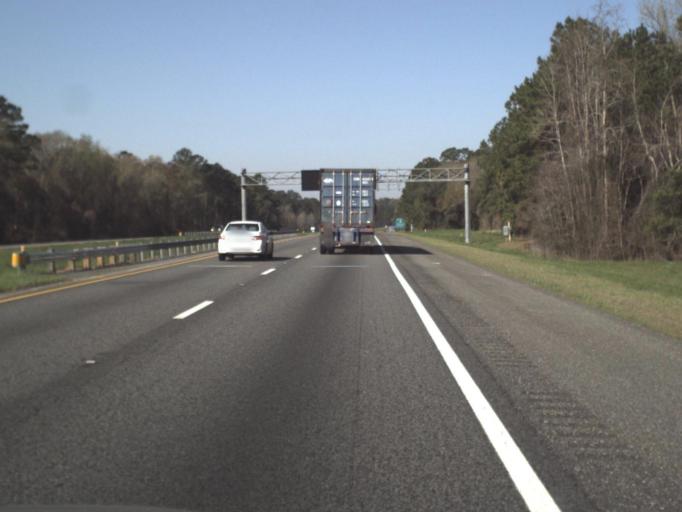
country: US
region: Florida
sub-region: Leon County
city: Tallahassee
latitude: 30.4784
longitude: -84.1340
